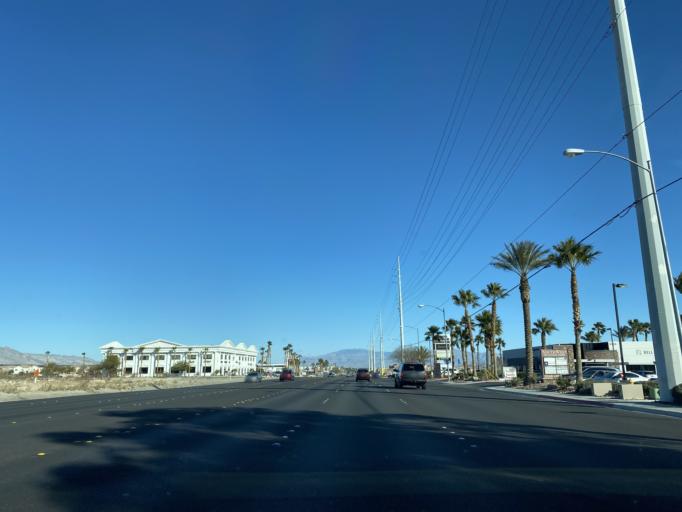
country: US
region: Nevada
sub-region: Clark County
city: Spring Valley
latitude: 36.0800
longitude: -115.2426
